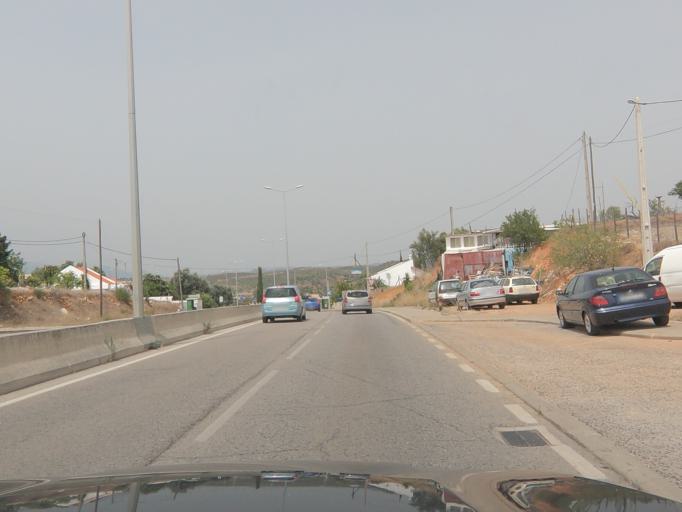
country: PT
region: Faro
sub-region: Portimao
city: Portimao
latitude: 37.1652
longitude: -8.5319
